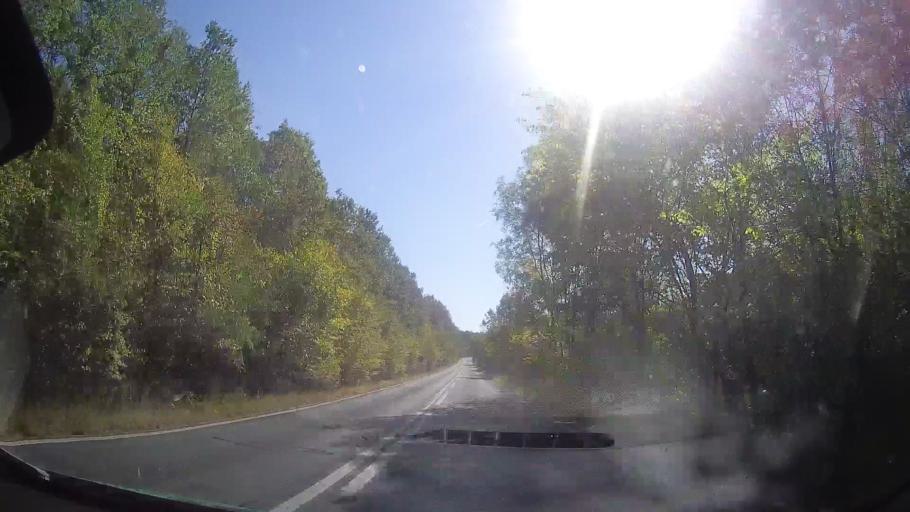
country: RO
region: Timis
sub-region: Comuna Barna
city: Barna
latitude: 45.7400
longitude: 21.9958
